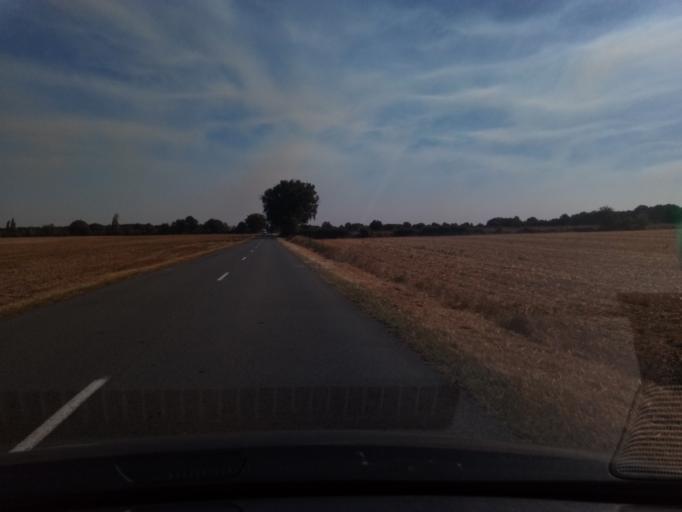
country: FR
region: Poitou-Charentes
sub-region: Departement de la Vienne
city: Montmorillon
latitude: 46.4921
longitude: 0.7840
